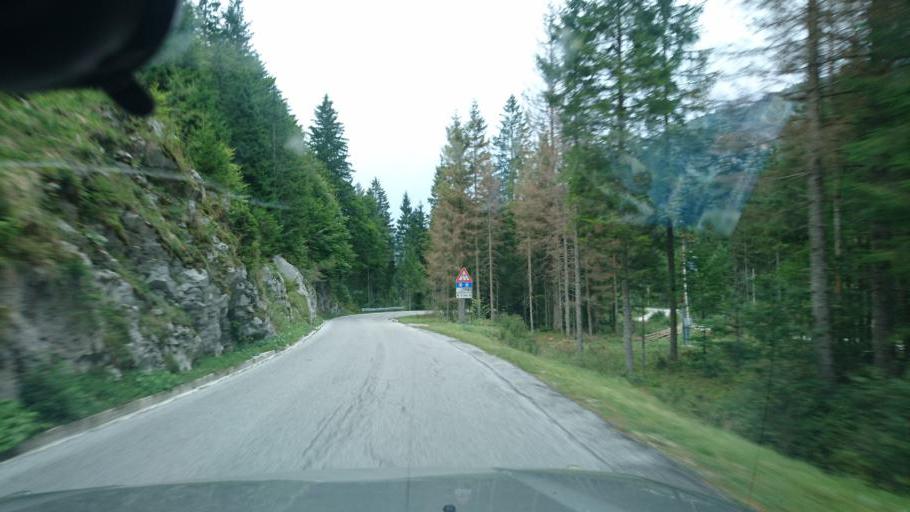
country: IT
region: Friuli Venezia Giulia
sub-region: Provincia di Udine
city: Malborghetto
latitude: 46.4700
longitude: 13.4915
